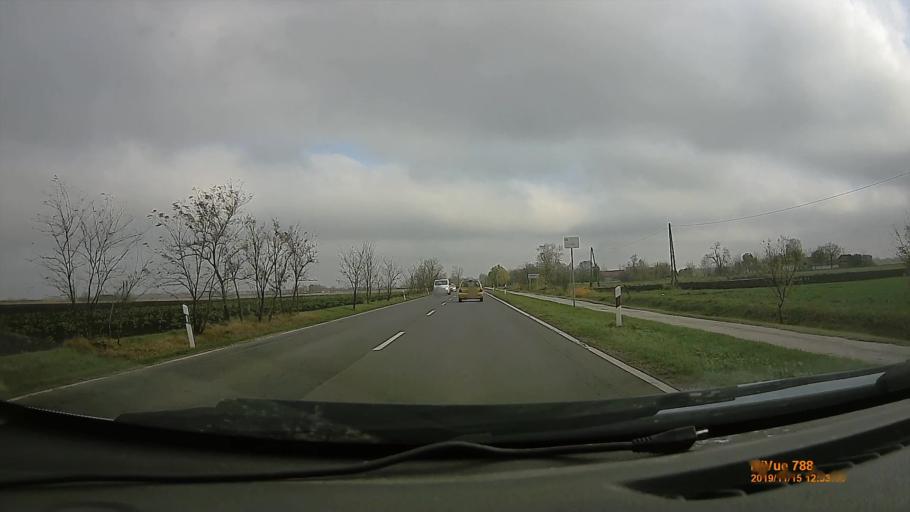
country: HU
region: Bekes
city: Kondoros
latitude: 46.7413
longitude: 20.8784
